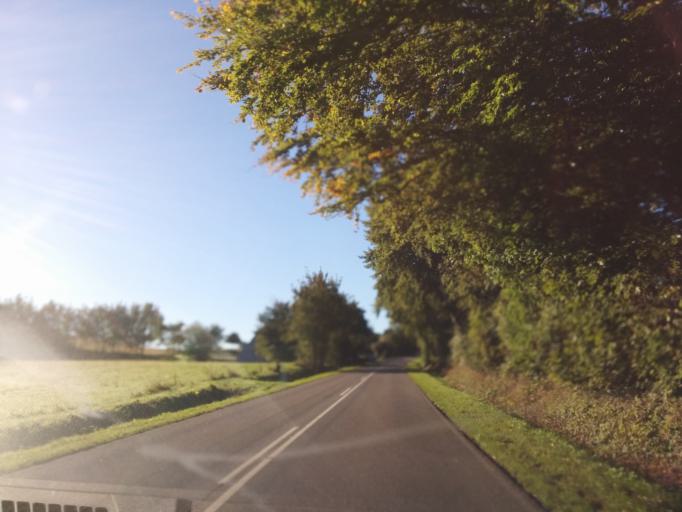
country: DK
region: South Denmark
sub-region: Kolding Kommune
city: Sonder Bjert
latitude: 55.4200
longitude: 9.5619
